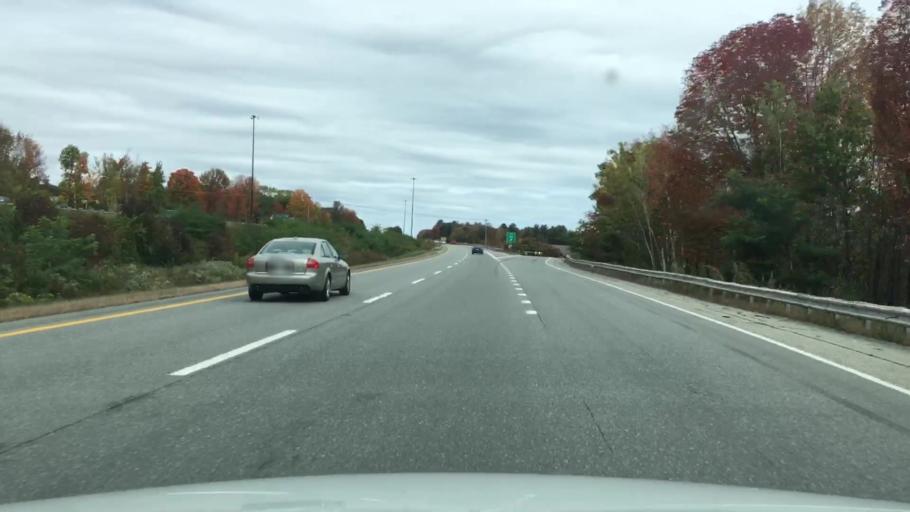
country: US
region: Maine
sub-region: Kennebec County
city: Oakland
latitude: 44.5421
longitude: -69.6814
